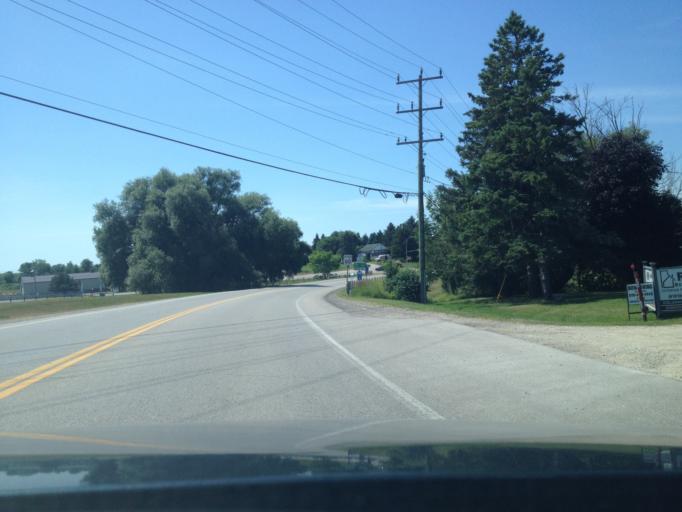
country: CA
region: Ontario
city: Waterloo
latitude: 43.5129
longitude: -80.5549
